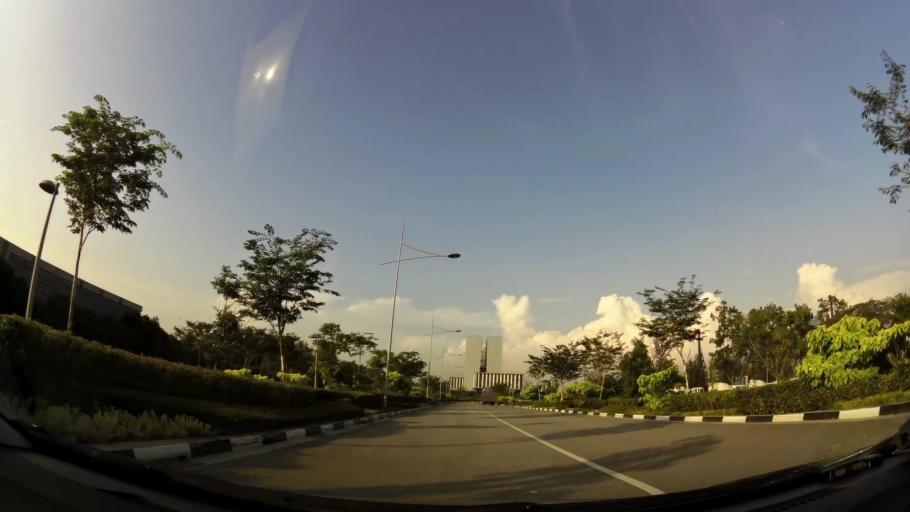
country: SG
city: Singapore
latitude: 1.2767
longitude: 103.8691
